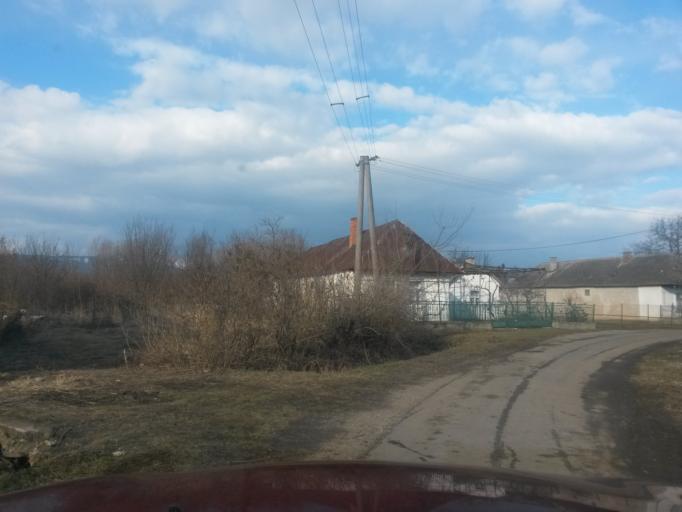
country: SK
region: Kosicky
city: Sobrance
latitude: 48.7751
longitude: 22.0846
